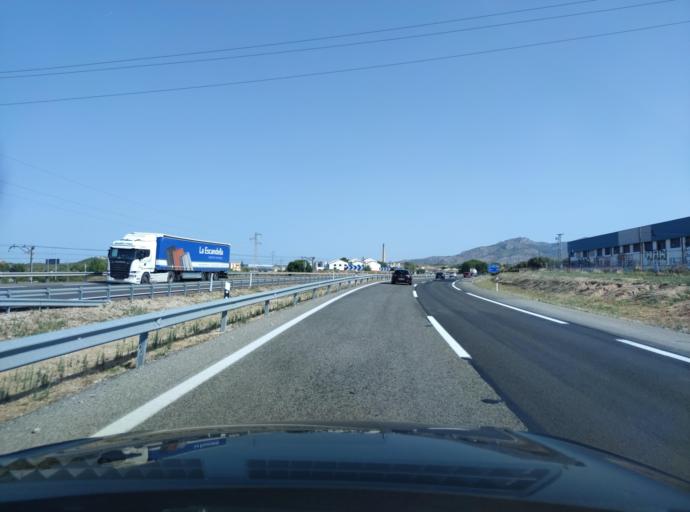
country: ES
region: Valencia
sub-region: Provincia de Alicante
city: Sax
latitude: 38.5401
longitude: -0.8110
